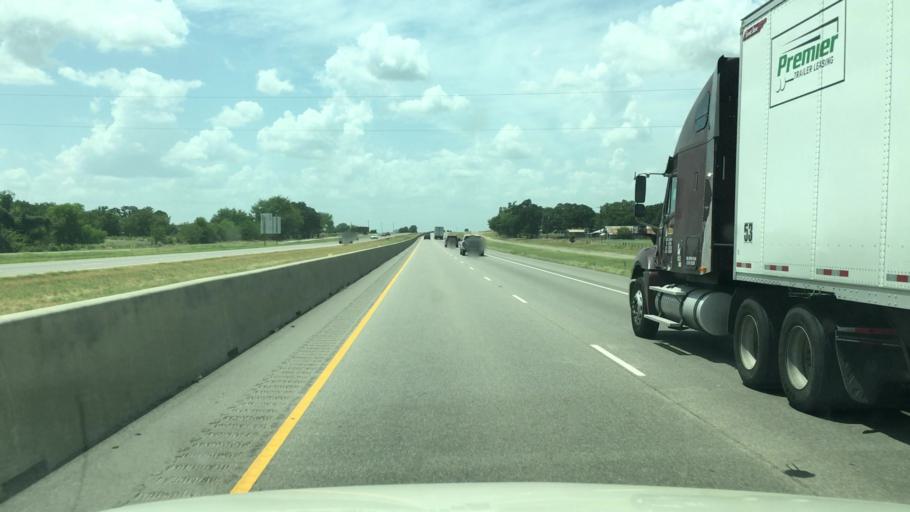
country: US
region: Texas
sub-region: Franklin County
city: Mount Vernon
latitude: 33.1633
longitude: -95.2579
